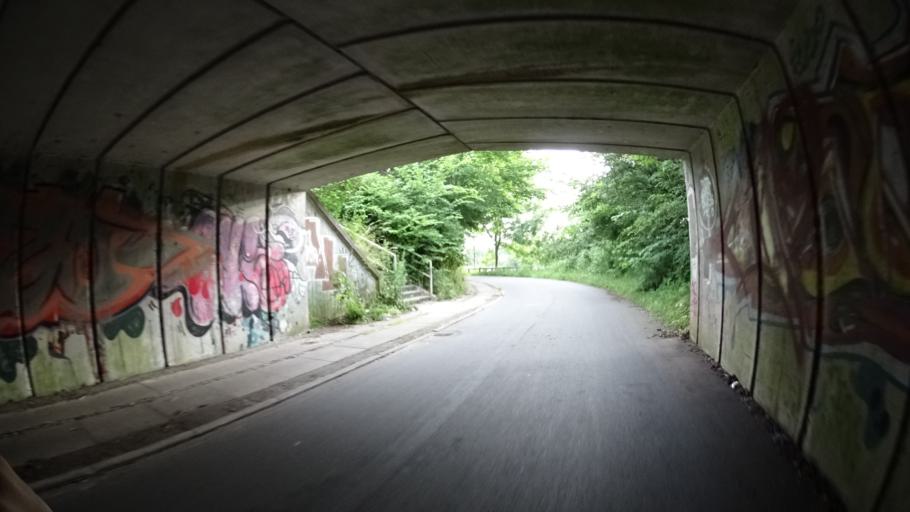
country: DK
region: Central Jutland
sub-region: Arhus Kommune
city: Stavtrup
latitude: 56.1403
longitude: 10.1545
